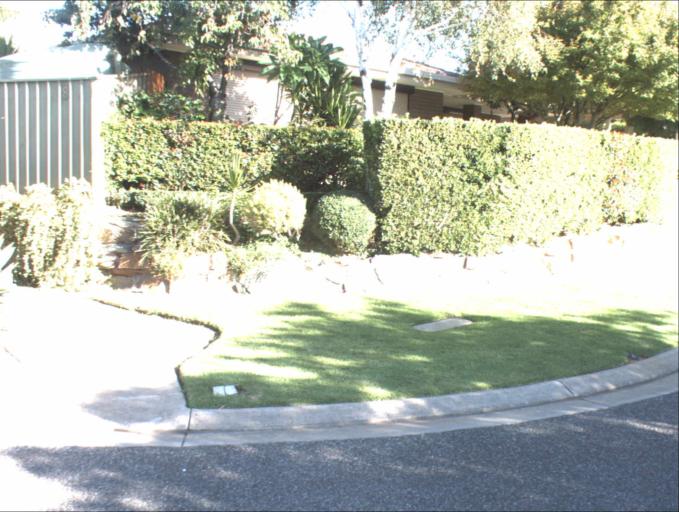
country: AU
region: South Australia
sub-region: Campbelltown
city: Paradise
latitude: -34.8718
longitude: 138.6528
